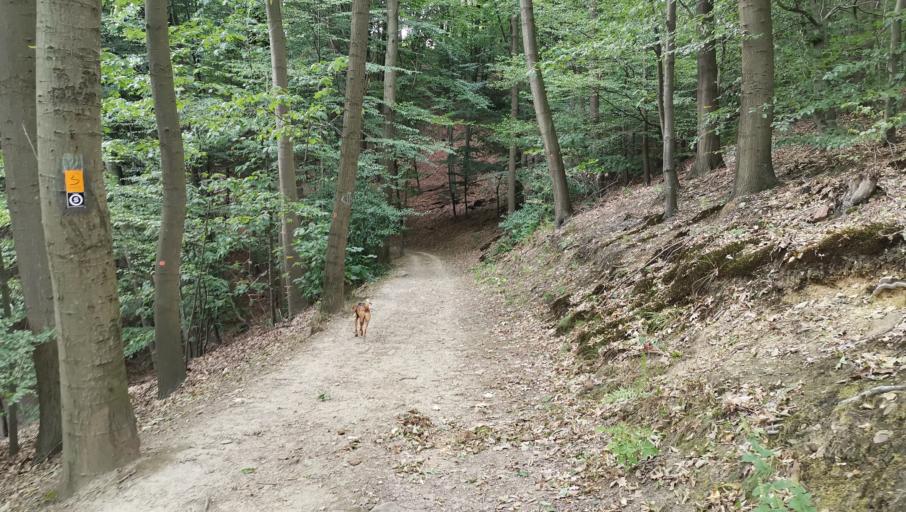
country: DE
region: North Rhine-Westphalia
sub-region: Regierungsbezirk Dusseldorf
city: Solingen
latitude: 51.1605
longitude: 7.1299
